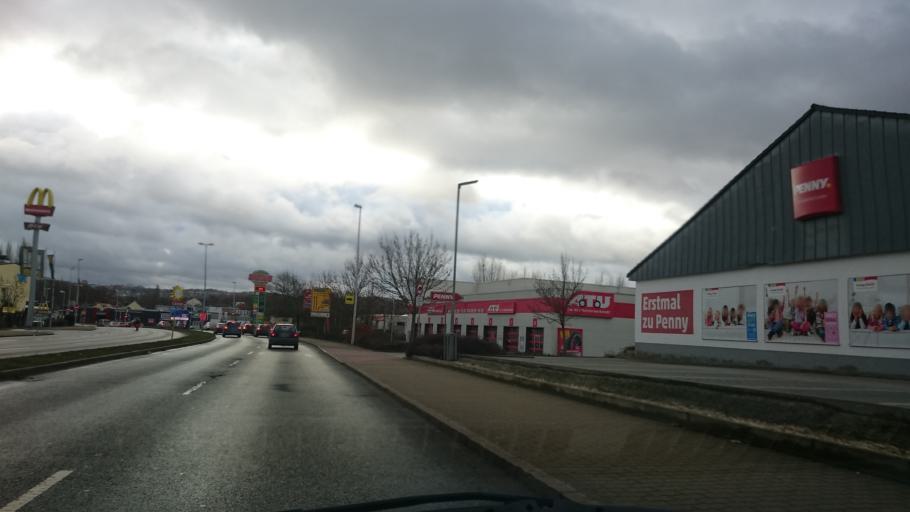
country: DE
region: Saxony
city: Zwickau
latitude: 50.7070
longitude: 12.5009
